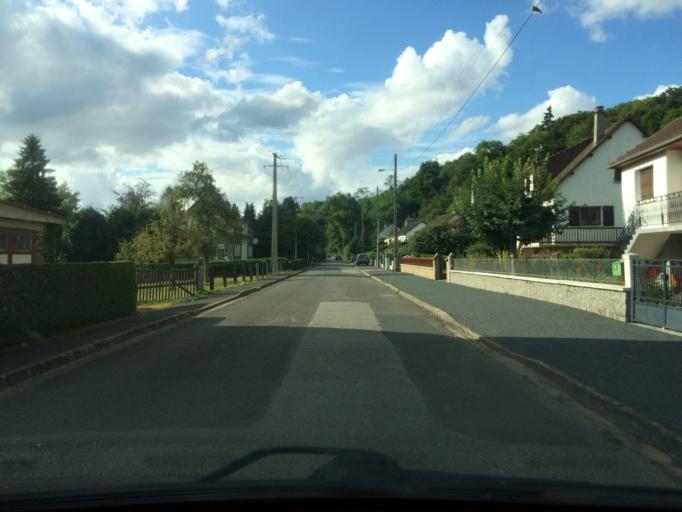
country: FR
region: Lower Normandy
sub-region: Departement du Calvados
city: Clecy
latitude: 48.8761
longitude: -0.4112
